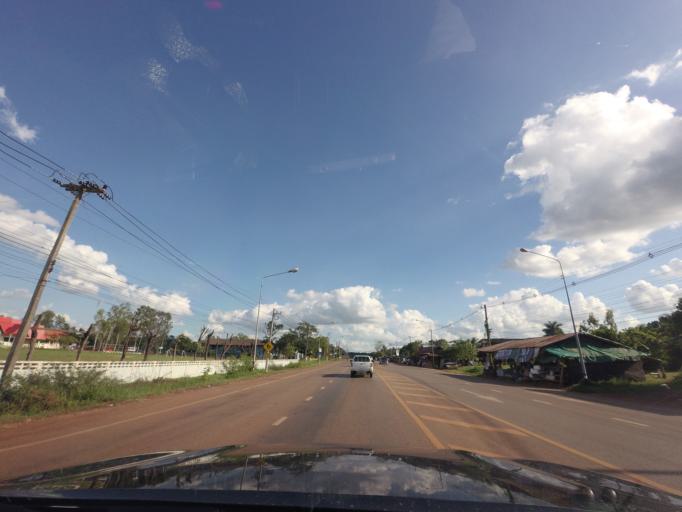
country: TH
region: Changwat Udon Thani
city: Ban Dung
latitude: 17.7092
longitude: 103.2506
